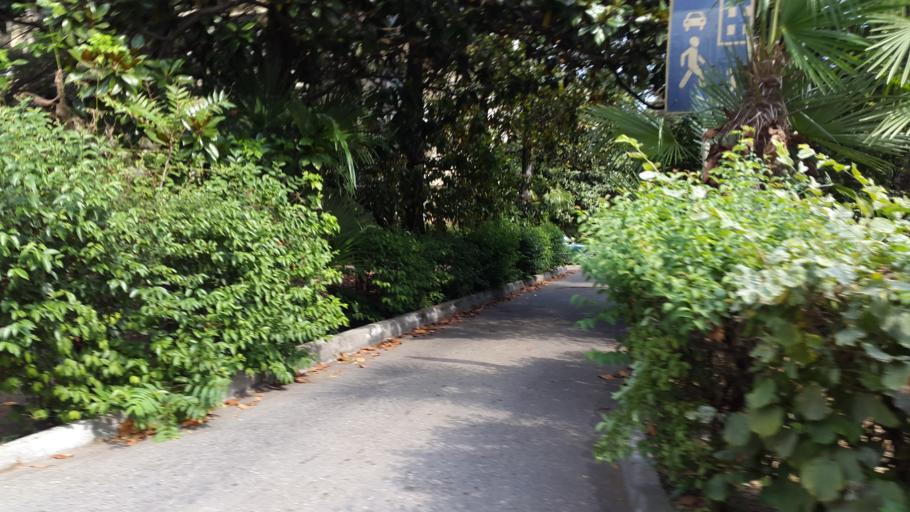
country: RU
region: Krasnodarskiy
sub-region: Sochi City
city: Sochi
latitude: 43.6000
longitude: 39.7221
